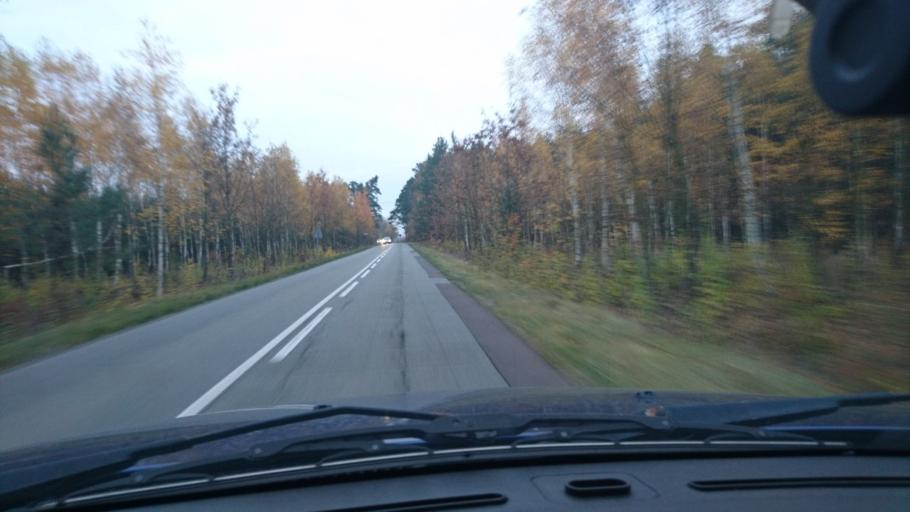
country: PL
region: Greater Poland Voivodeship
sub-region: Powiat ostrowski
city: Odolanow
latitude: 51.5290
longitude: 17.6500
